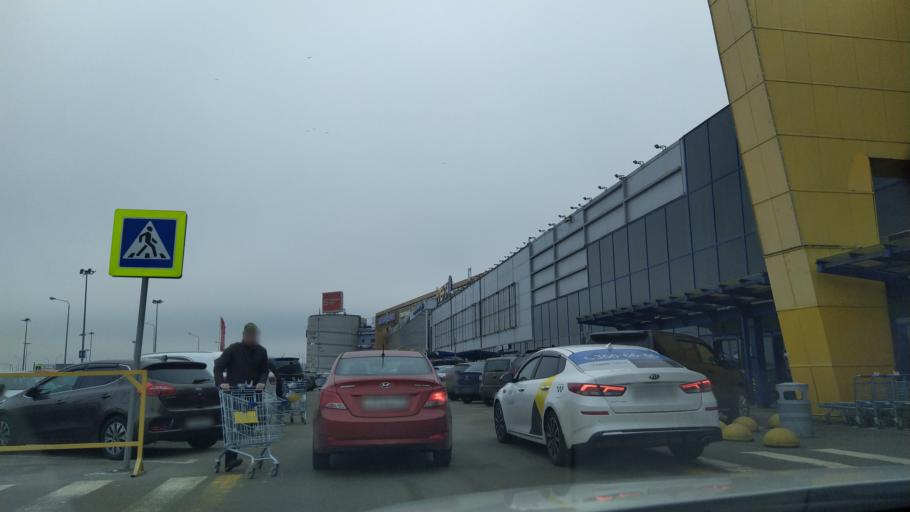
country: RU
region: St.-Petersburg
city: Kupchino
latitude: 59.8085
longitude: 30.3212
